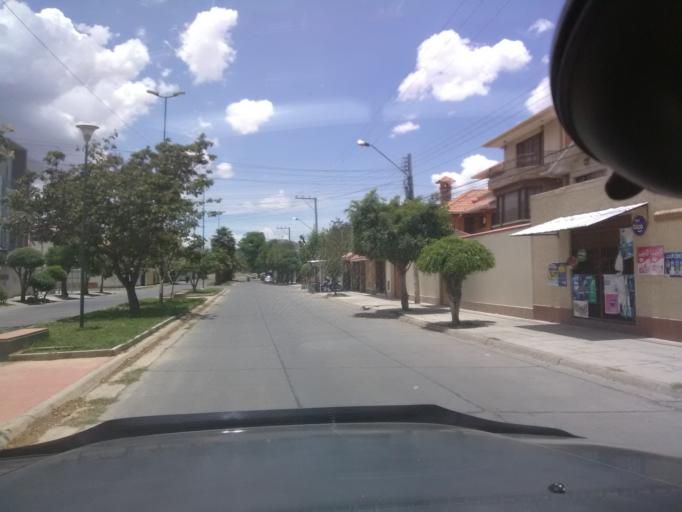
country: BO
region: Cochabamba
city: Cochabamba
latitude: -17.3793
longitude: -66.1777
